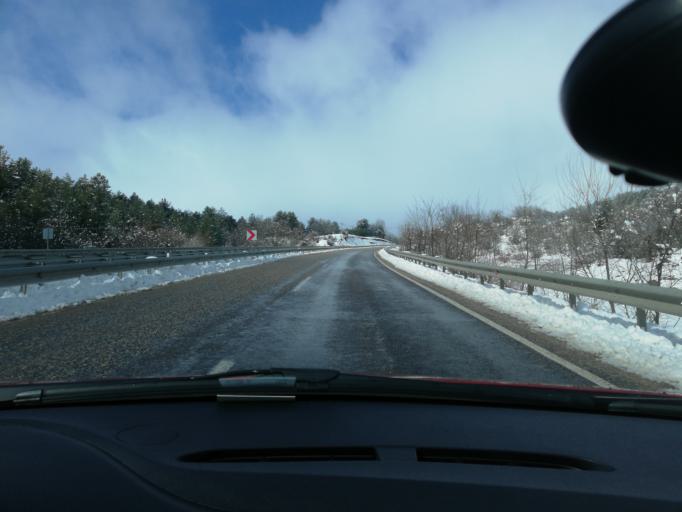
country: TR
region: Kastamonu
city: Ihsangazi
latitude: 41.3050
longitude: 33.5825
